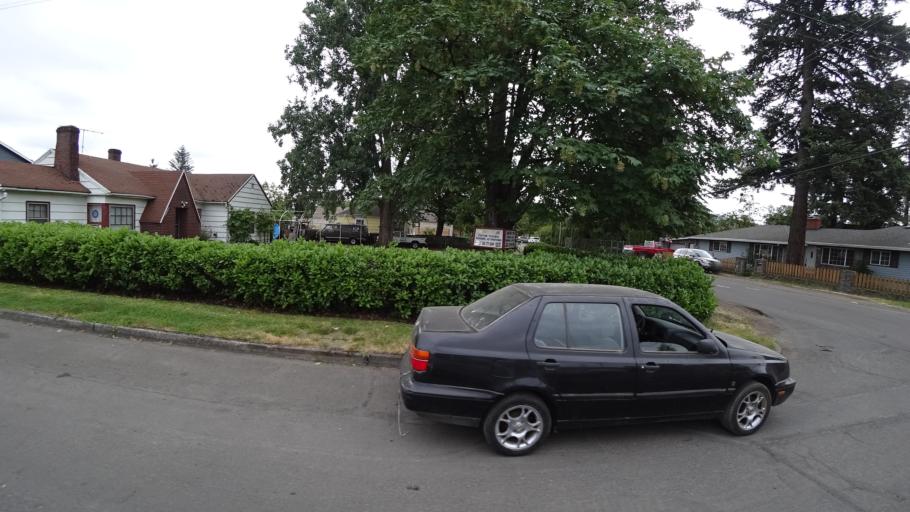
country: US
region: Oregon
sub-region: Multnomah County
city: Lents
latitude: 45.4711
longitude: -122.5856
